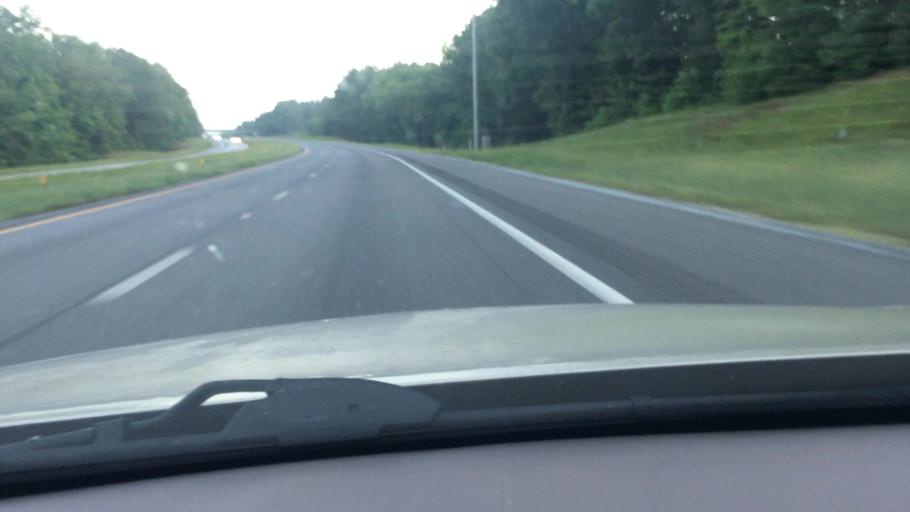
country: US
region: South Carolina
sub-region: Lexington County
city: Irmo
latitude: 34.1334
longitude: -81.2106
